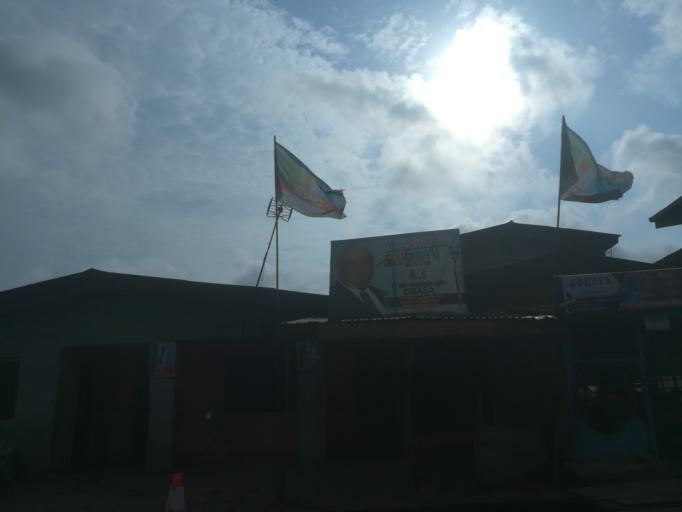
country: NG
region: Lagos
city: Agege
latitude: 6.6185
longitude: 3.3130
